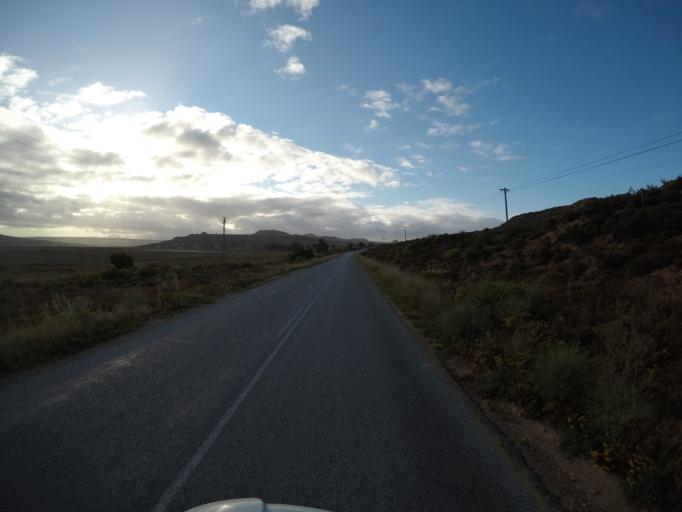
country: ZA
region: Western Cape
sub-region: West Coast District Municipality
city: Clanwilliam
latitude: -32.3255
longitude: 18.3658
